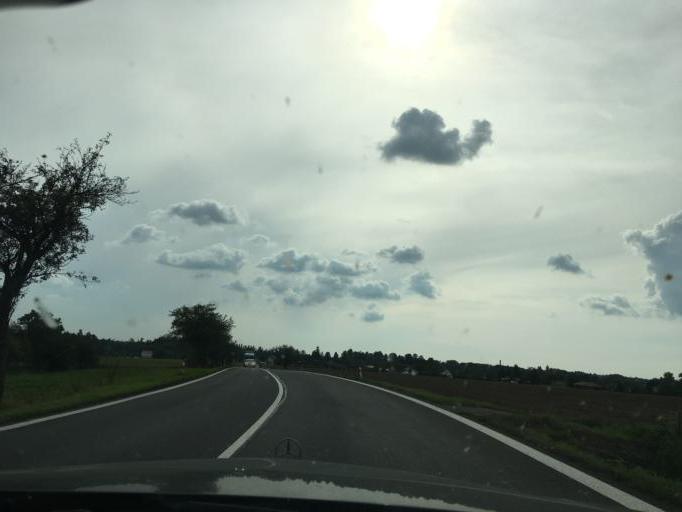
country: CZ
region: Kralovehradecky
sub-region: Okres Nachod
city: Jaromer
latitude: 50.3723
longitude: 15.9410
